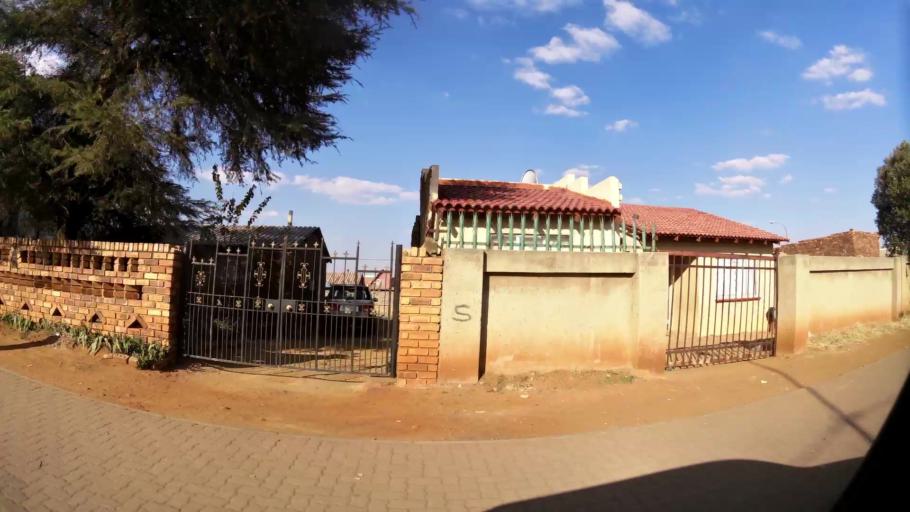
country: ZA
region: Gauteng
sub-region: City of Johannesburg Metropolitan Municipality
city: Roodepoort
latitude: -26.2159
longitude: 27.8755
